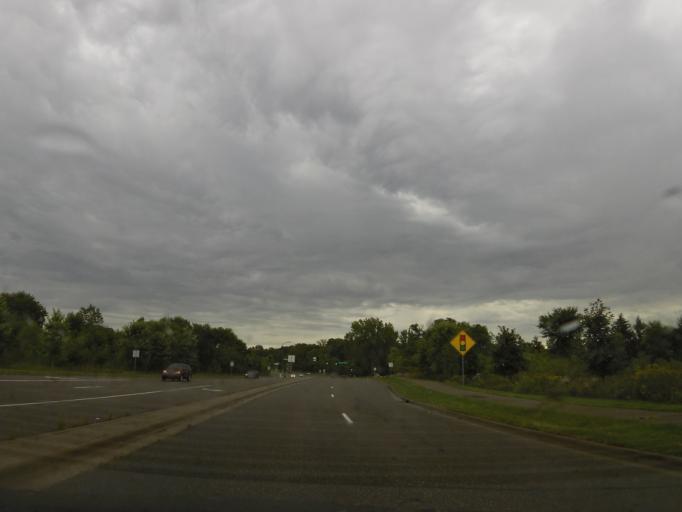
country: US
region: Minnesota
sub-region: Washington County
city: Woodbury
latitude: 44.9390
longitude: -92.9215
